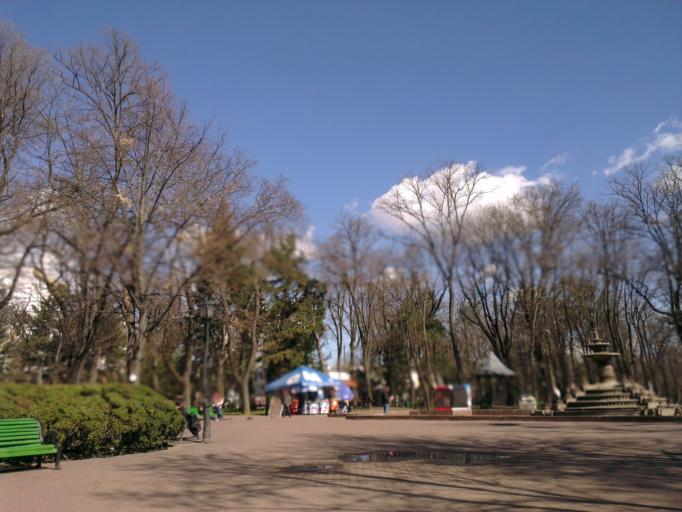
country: MD
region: Chisinau
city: Chisinau
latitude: 47.0253
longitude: 28.8279
